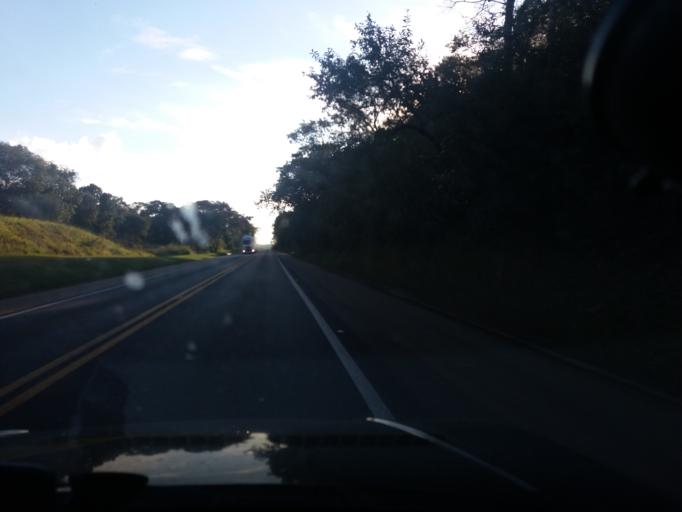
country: BR
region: Sao Paulo
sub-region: Buri
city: Buri
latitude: -23.9322
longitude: -48.6373
